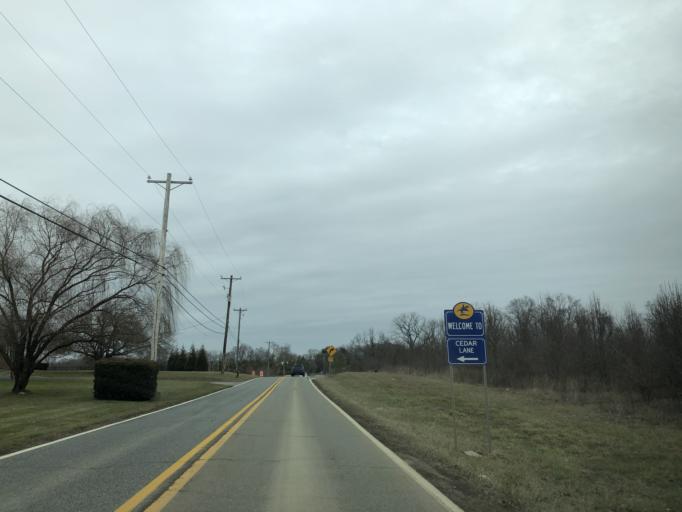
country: US
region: Delaware
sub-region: New Castle County
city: Middletown
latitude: 39.4873
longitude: -75.6947
